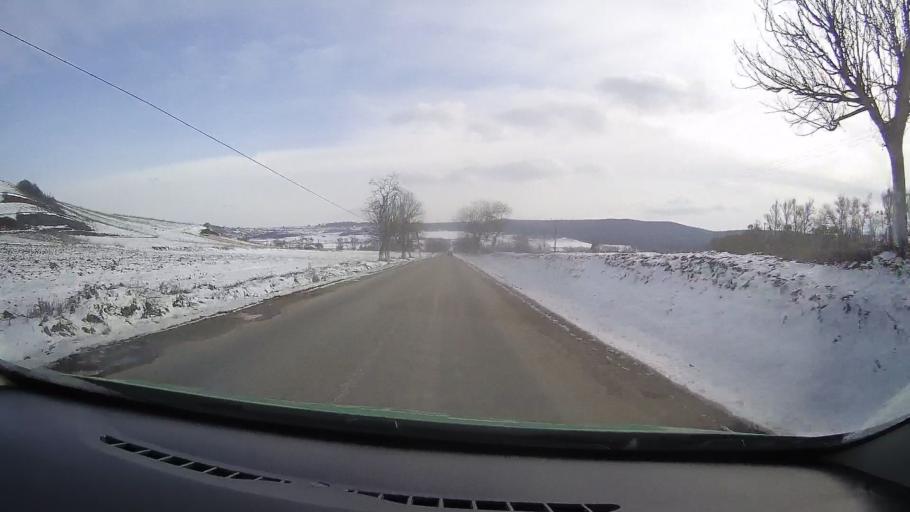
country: RO
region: Sibiu
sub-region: Comuna Iacobeni
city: Iacobeni
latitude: 46.0431
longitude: 24.7285
